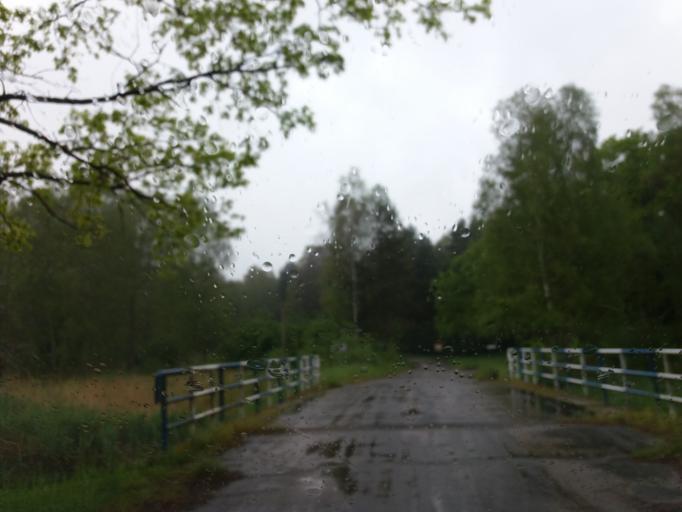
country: PL
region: West Pomeranian Voivodeship
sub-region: Powiat drawski
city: Kalisz Pomorski
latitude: 53.2081
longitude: 15.9684
